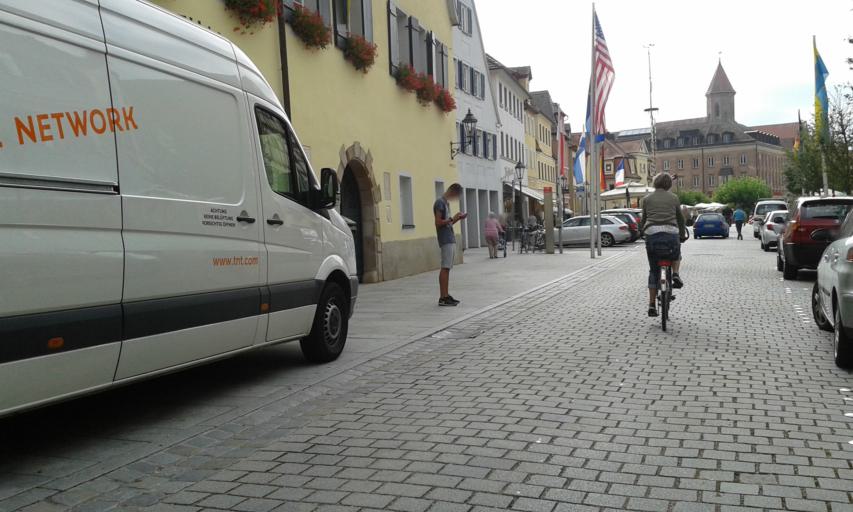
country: DE
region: Bavaria
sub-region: Regierungsbezirk Mittelfranken
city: Gunzenhausen
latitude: 49.1147
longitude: 10.7540
